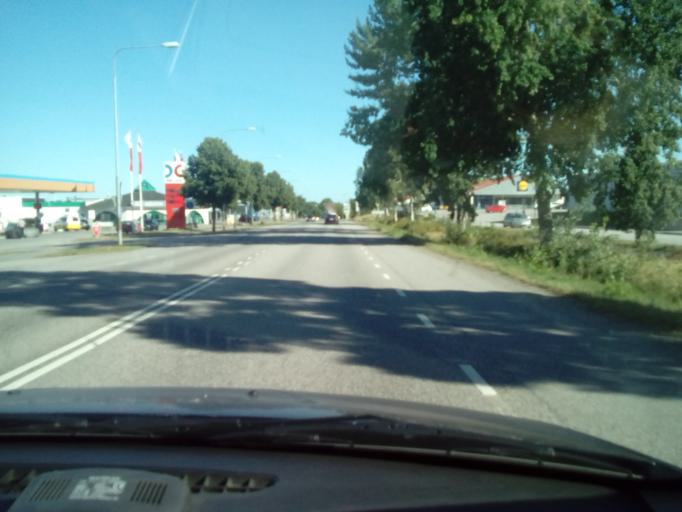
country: SE
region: Kalmar
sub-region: Vasterviks Kommun
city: Vaestervik
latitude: 57.7615
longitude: 16.6095
